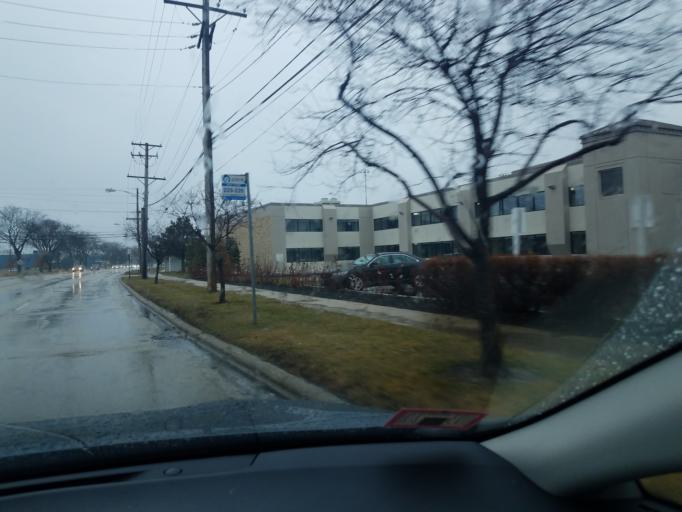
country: US
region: Illinois
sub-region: Cook County
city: Lincolnwood
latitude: 42.0125
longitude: -87.7614
